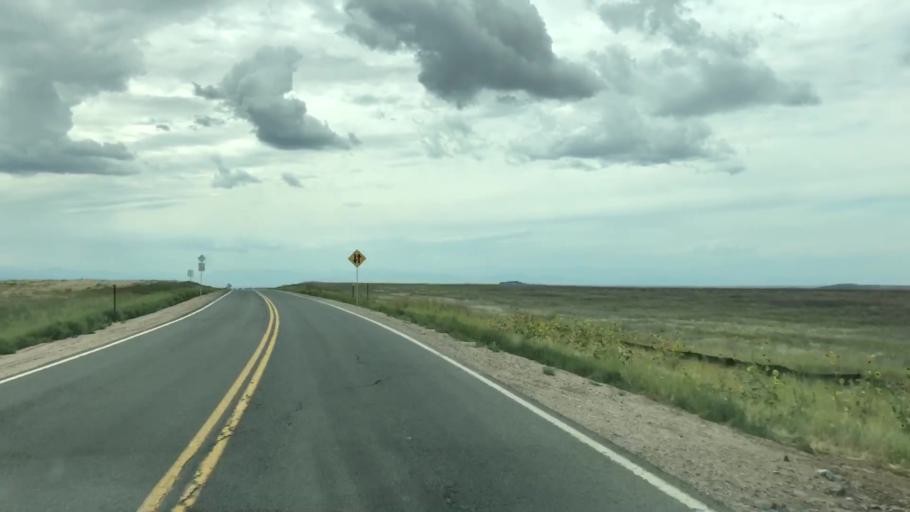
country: US
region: Colorado
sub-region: Adams County
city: Aurora
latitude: 39.7984
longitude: -104.6801
